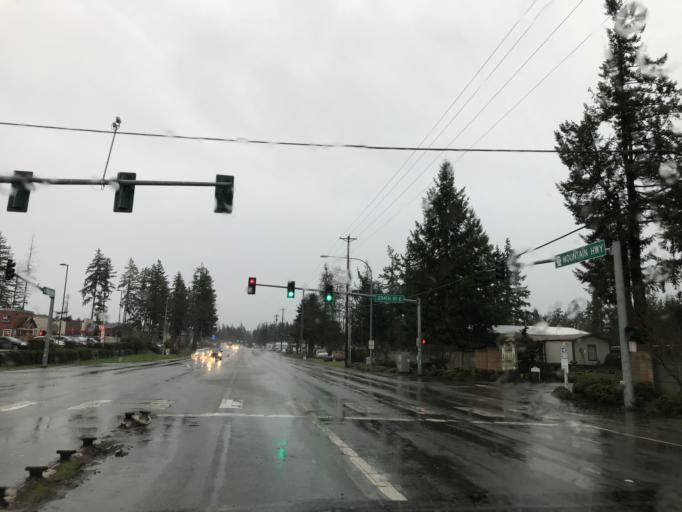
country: US
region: Washington
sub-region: Pierce County
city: Elk Plain
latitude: 47.0716
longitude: -122.4190
